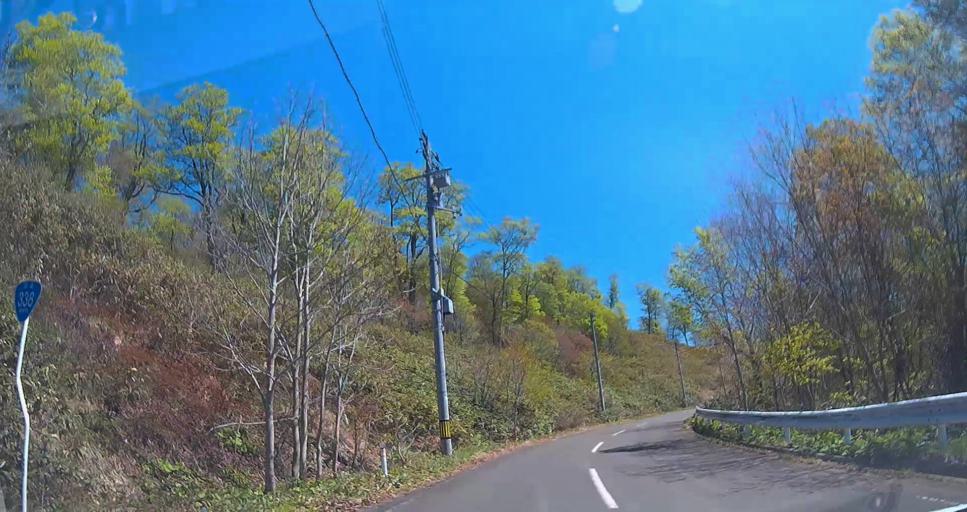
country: JP
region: Aomori
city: Mutsu
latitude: 41.2310
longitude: 140.8135
